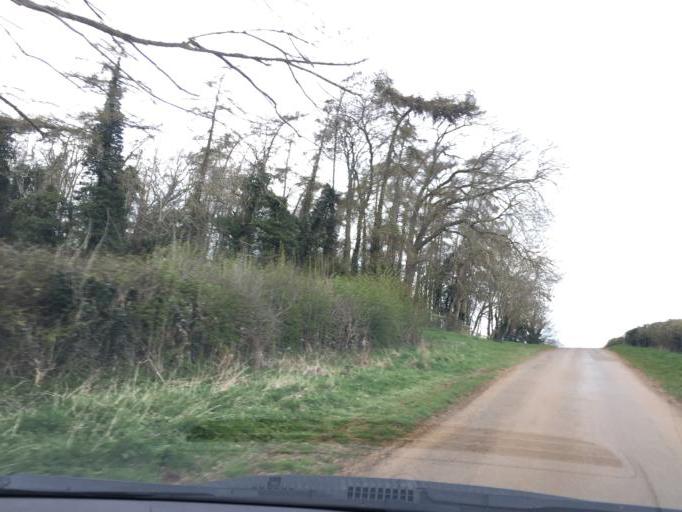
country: GB
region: England
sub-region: Oxfordshire
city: Hanwell
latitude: 52.0839
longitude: -1.3921
